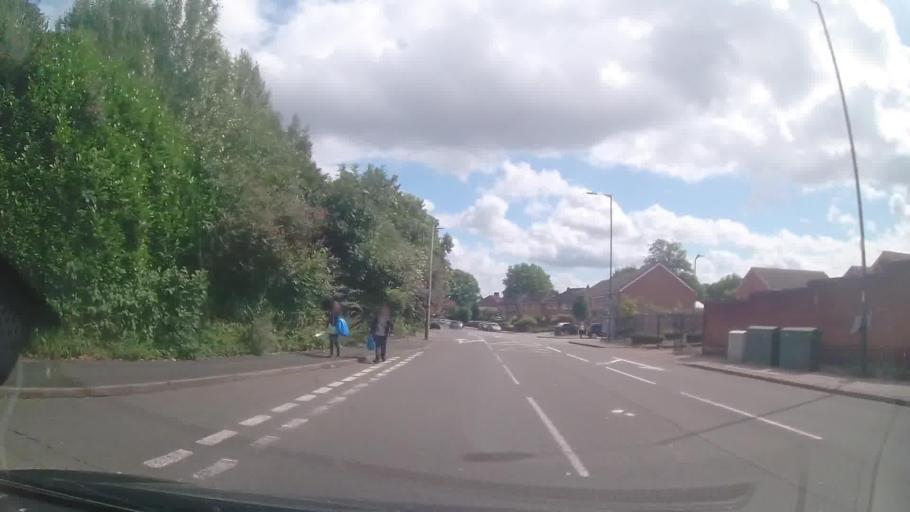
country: GB
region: England
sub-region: Walsall
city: Darlaston
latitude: 52.5704
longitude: -2.0185
